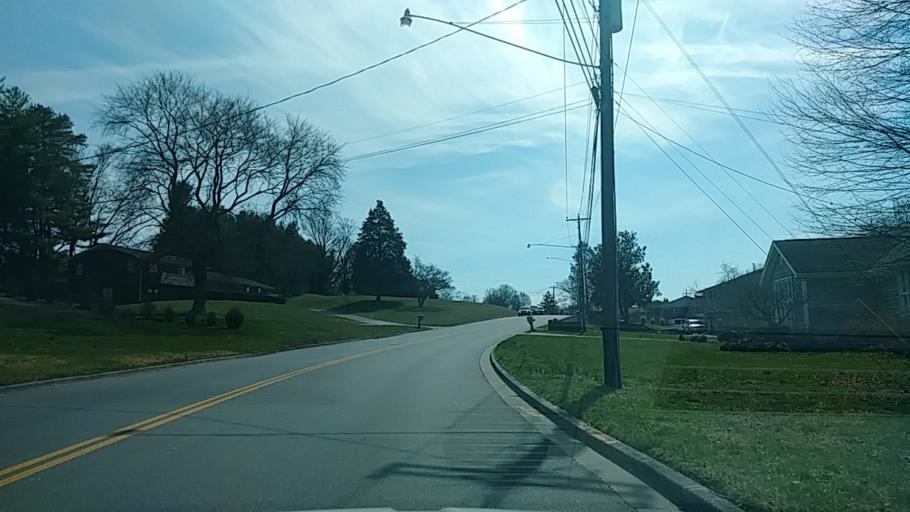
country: US
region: Tennessee
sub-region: Hamblen County
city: Morristown
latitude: 36.2160
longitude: -83.3203
